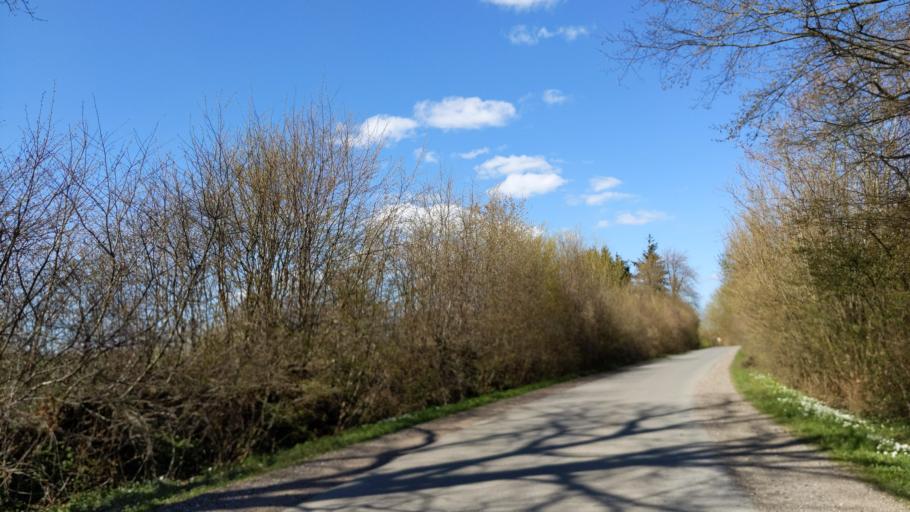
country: DE
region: Schleswig-Holstein
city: Susel
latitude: 54.1136
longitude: 10.6835
